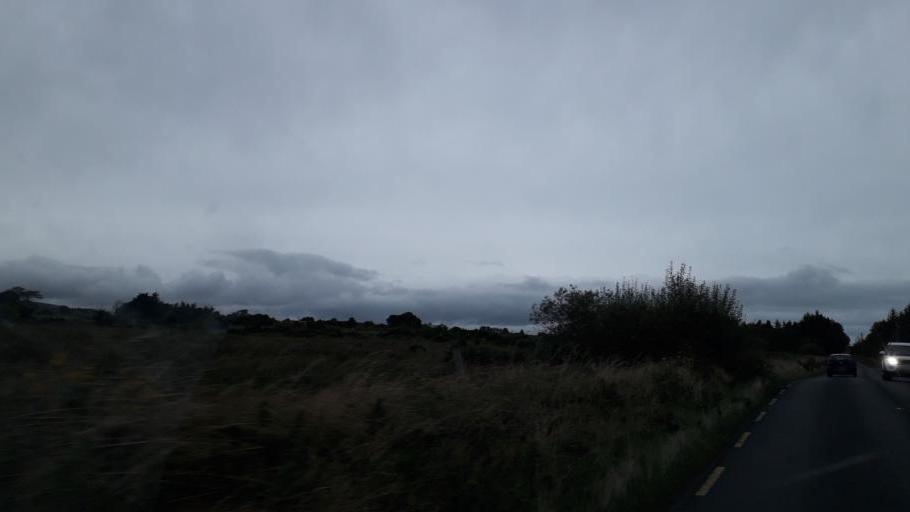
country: IE
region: Leinster
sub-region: Wicklow
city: Kilmacanoge
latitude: 53.1216
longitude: -6.1846
